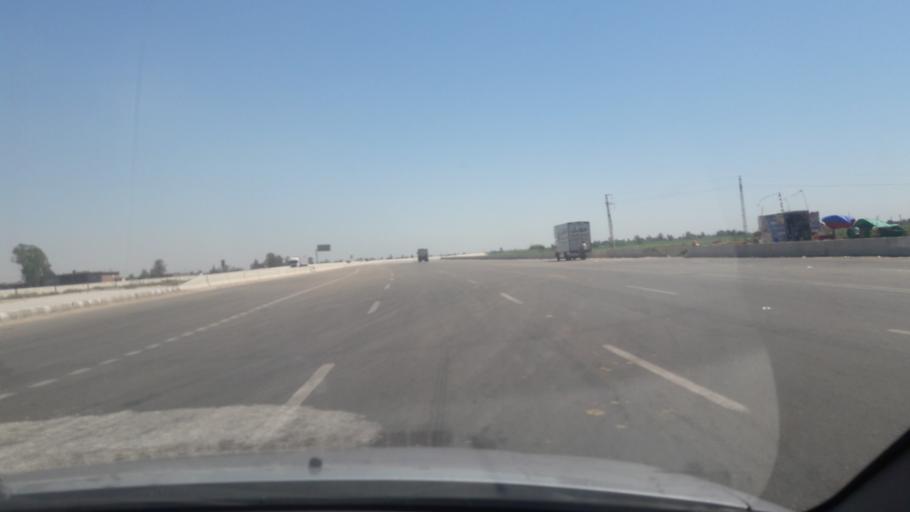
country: EG
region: Muhafazat Bur Sa`id
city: Port Said
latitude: 31.1026
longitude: 32.2334
